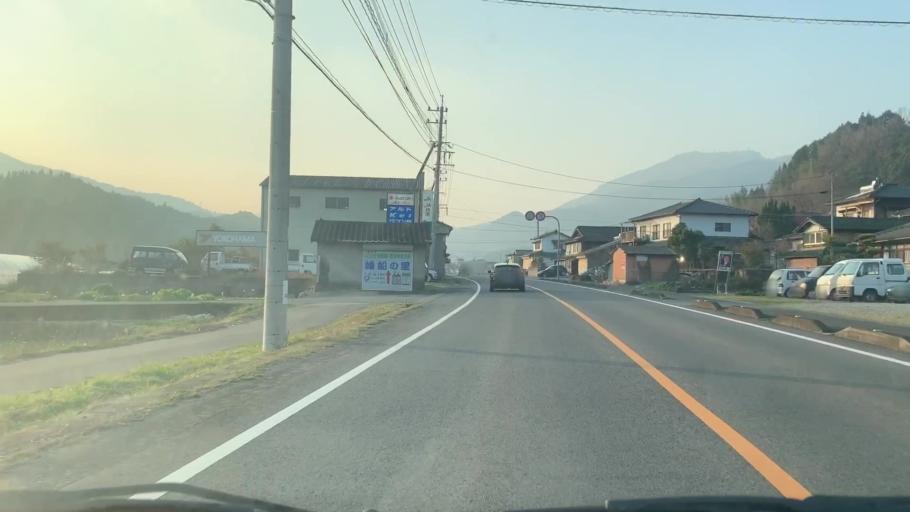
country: JP
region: Saga Prefecture
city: Takeocho-takeo
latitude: 33.2591
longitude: 130.0668
